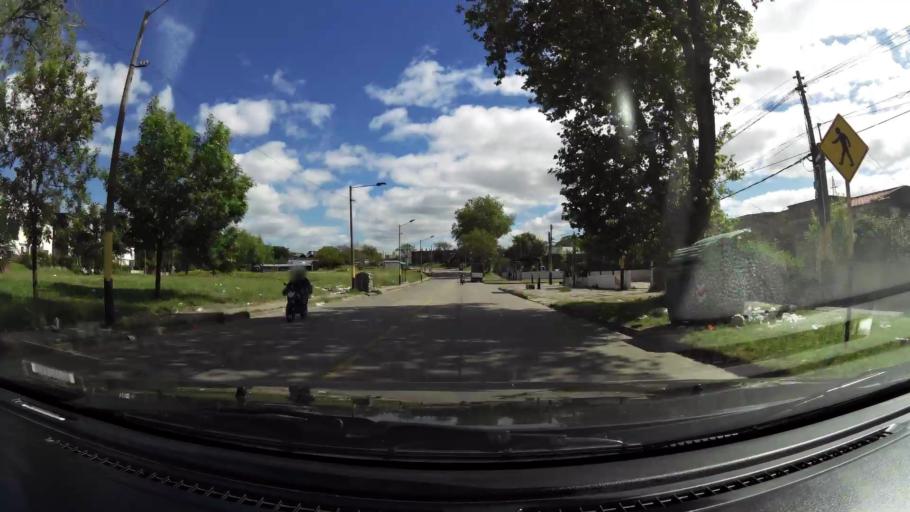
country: UY
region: Canelones
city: Paso de Carrasco
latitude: -34.8794
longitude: -56.1113
